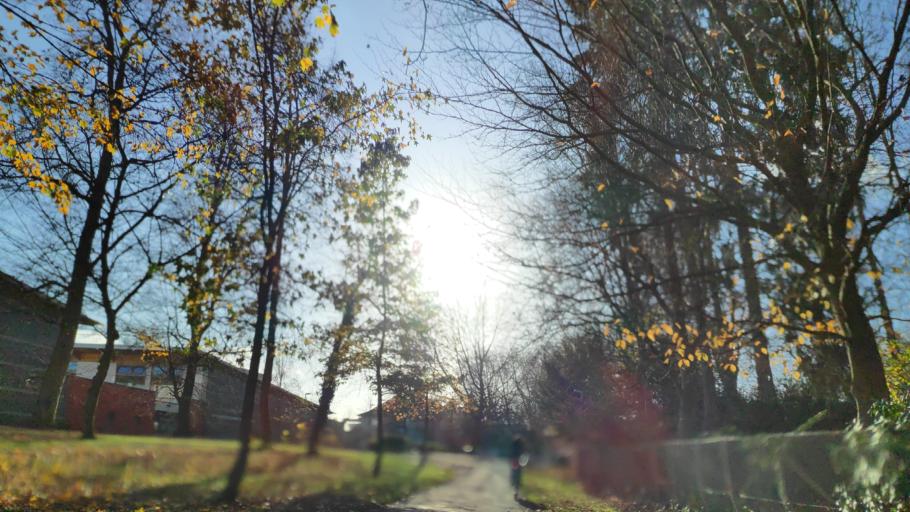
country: DE
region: North Rhine-Westphalia
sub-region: Regierungsbezirk Detmold
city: Minden
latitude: 52.2891
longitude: 8.9085
